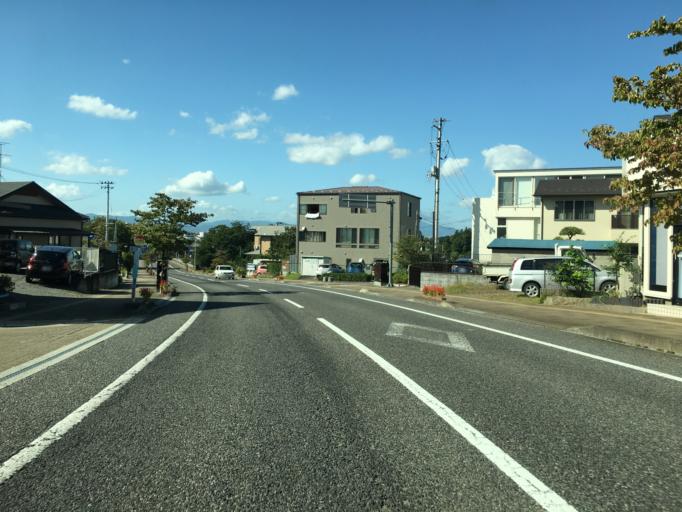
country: JP
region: Fukushima
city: Sukagawa
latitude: 37.2944
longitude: 140.3759
